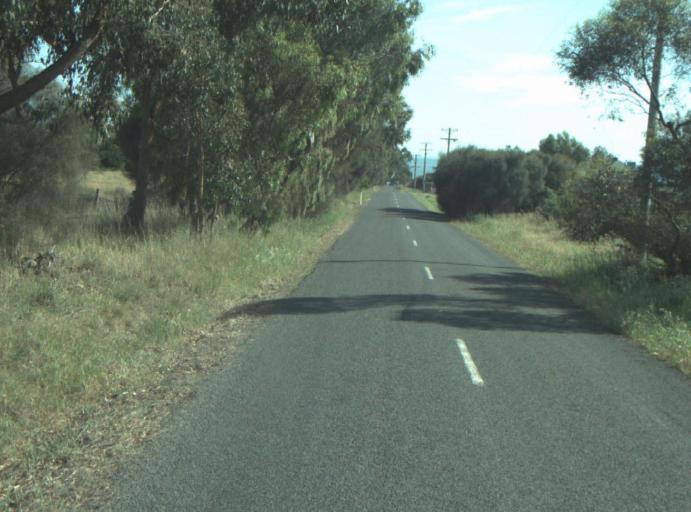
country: AU
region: Victoria
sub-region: Greater Geelong
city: Clifton Springs
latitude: -38.1649
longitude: 144.5162
